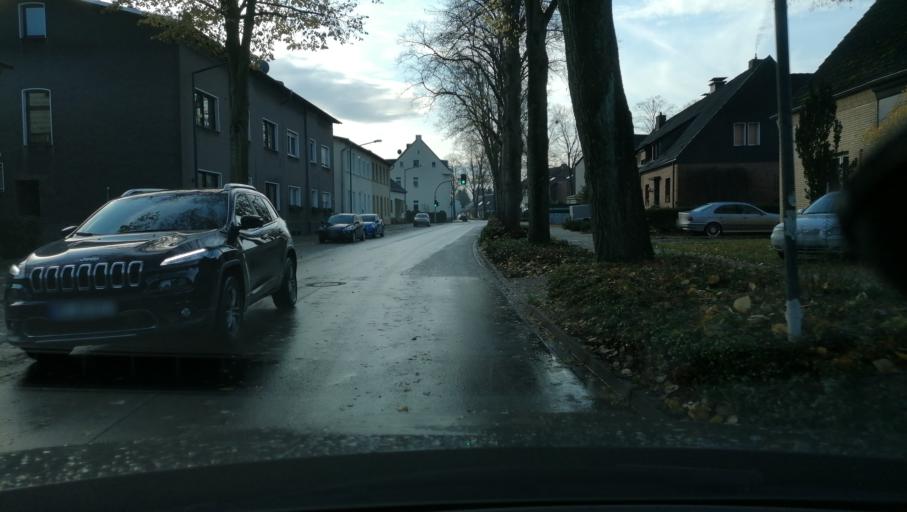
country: DE
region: North Rhine-Westphalia
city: Herten
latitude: 51.5960
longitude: 7.1511
